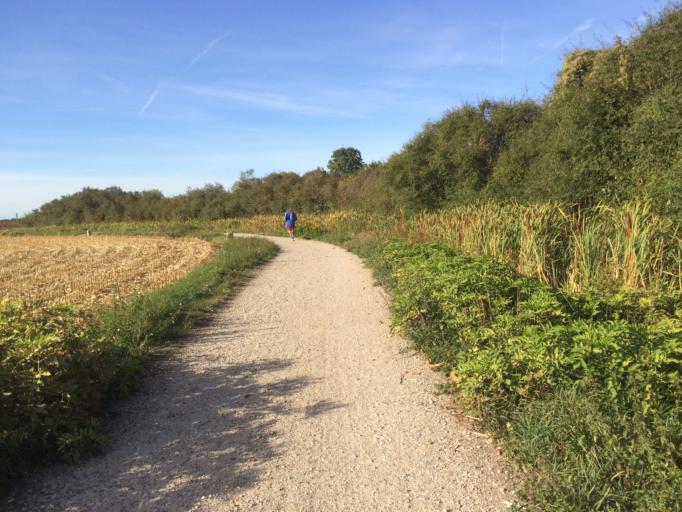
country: FR
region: Ile-de-France
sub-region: Departement de l'Essonne
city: Vauhallan
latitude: 48.7258
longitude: 2.1994
